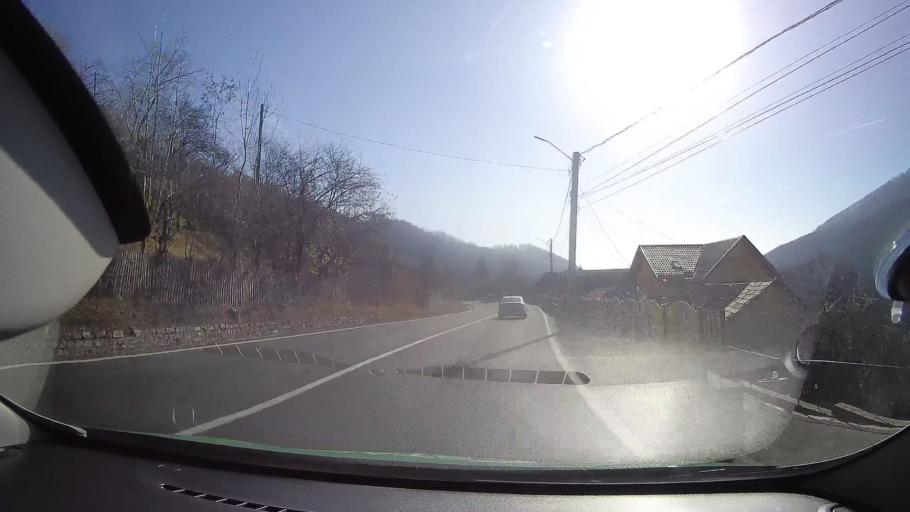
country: RO
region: Prahova
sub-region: Comuna Comarnic
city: Posada
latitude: 45.2889
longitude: 25.6151
